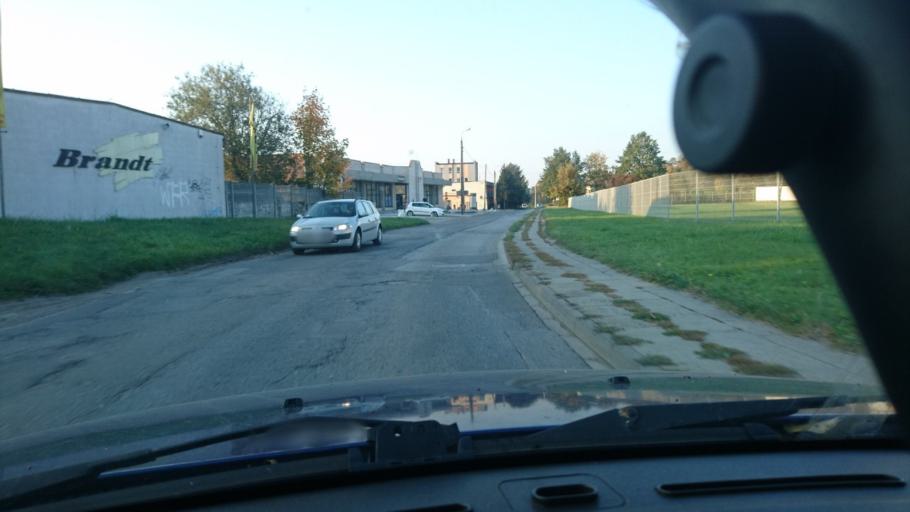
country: PL
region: Silesian Voivodeship
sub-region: Powiat bielski
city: Jaworze
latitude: 49.8138
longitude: 18.9828
